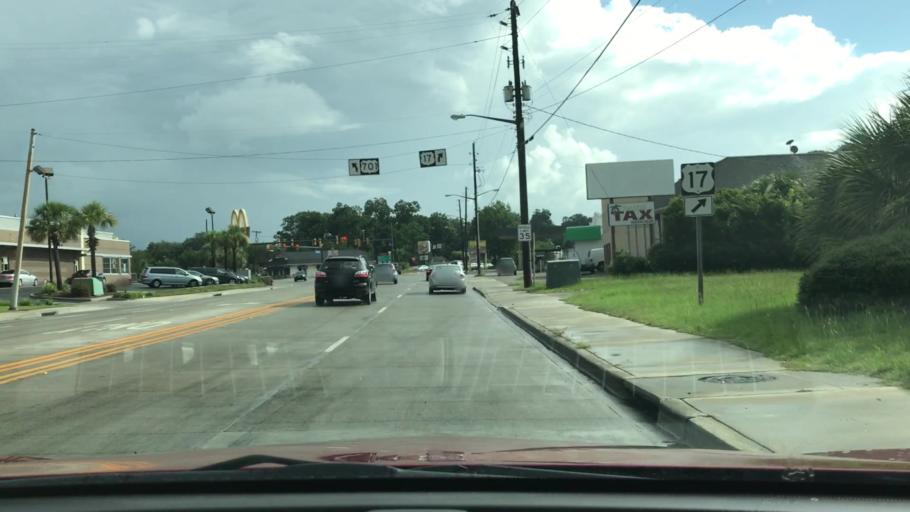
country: US
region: South Carolina
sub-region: Georgetown County
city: Georgetown
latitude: 33.3738
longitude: -79.2884
